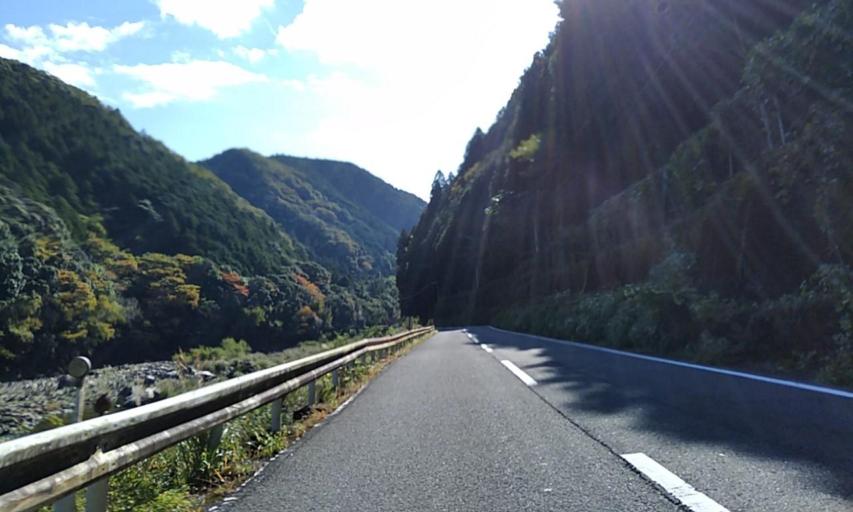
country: JP
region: Wakayama
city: Kainan
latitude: 34.0593
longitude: 135.3511
